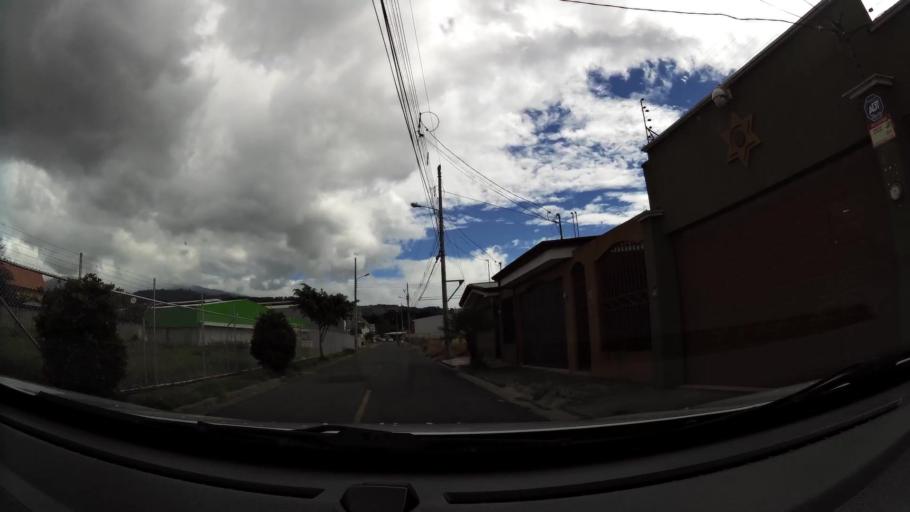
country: CR
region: Cartago
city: Concepcion
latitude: 9.9244
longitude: -84.0002
